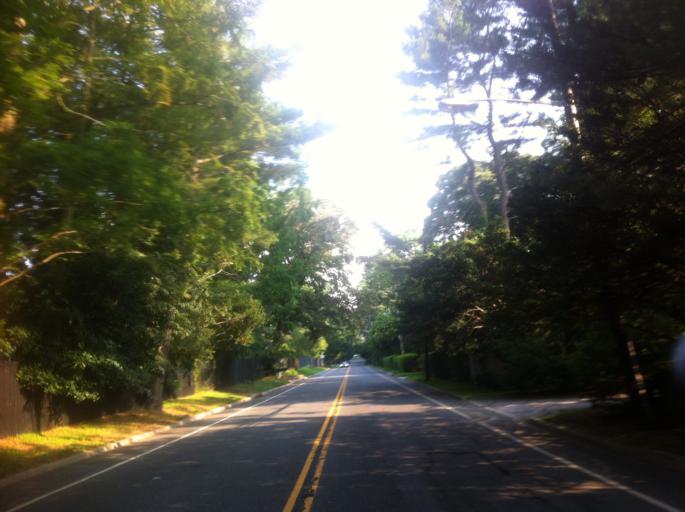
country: US
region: New York
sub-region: Nassau County
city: Lattingtown
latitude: 40.8893
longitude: -73.5862
